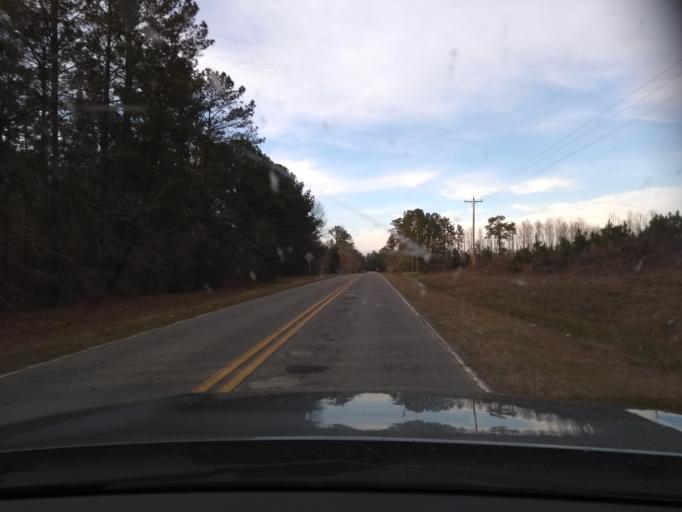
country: US
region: Georgia
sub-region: Evans County
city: Claxton
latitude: 32.2186
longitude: -81.7689
